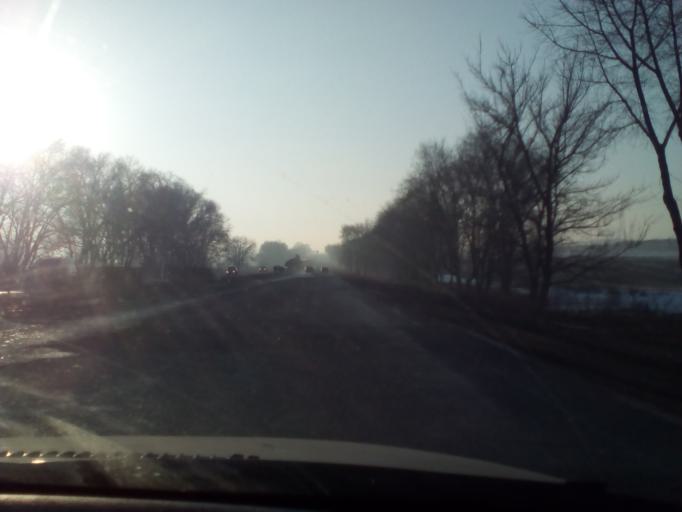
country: KZ
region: Almaty Oblysy
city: Burunday
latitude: 43.2232
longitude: 76.5893
